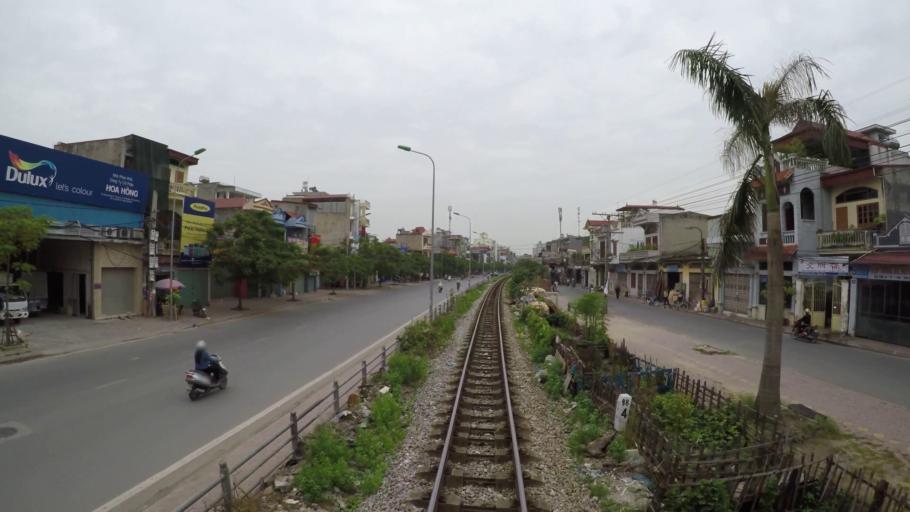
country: VN
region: Hai Phong
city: An Duong
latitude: 20.8748
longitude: 106.6395
